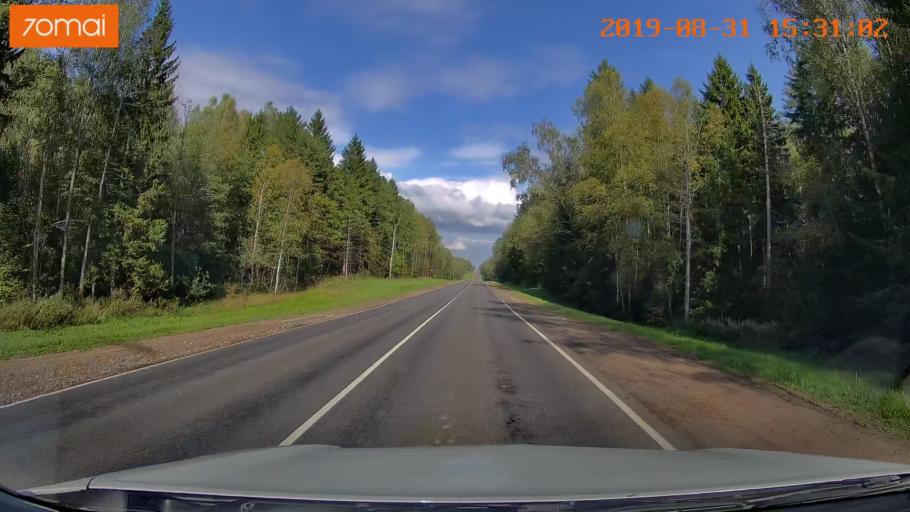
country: RU
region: Kaluga
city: Baryatino
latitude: 54.5796
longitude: 34.6445
